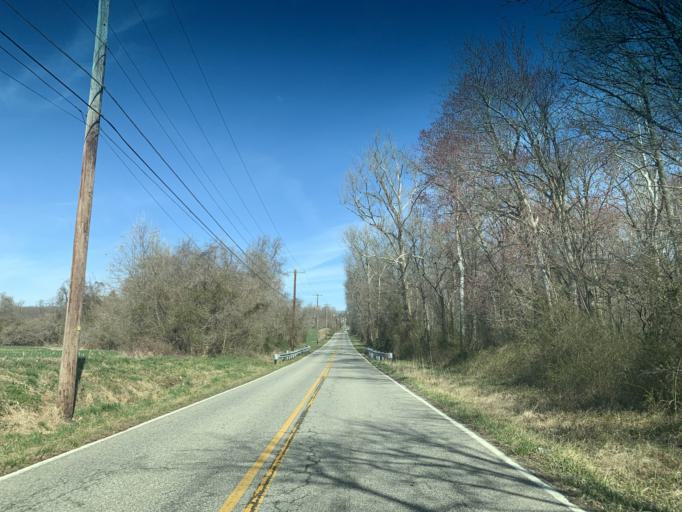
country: US
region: Maryland
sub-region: Cecil County
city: Charlestown
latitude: 39.5486
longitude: -76.0104
